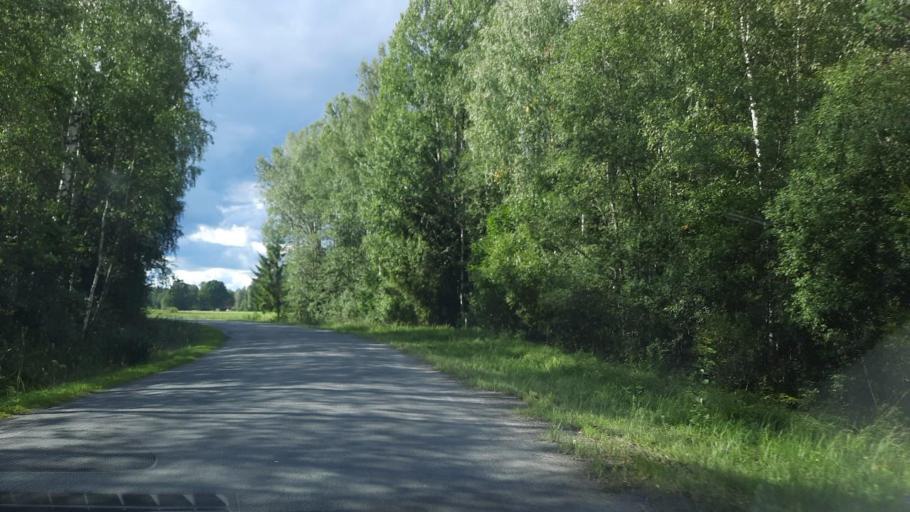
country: EE
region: Paernumaa
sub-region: Vaendra vald (alev)
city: Vandra
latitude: 58.4905
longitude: 24.9782
